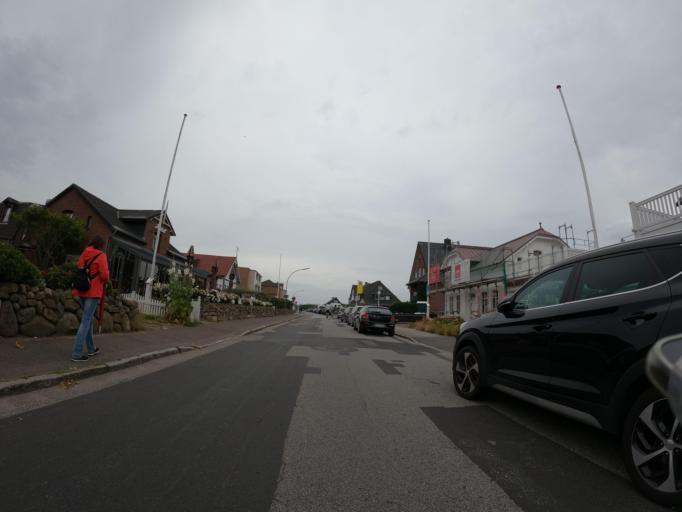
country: DE
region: Schleswig-Holstein
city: Westerland
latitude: 54.9378
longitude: 8.3221
